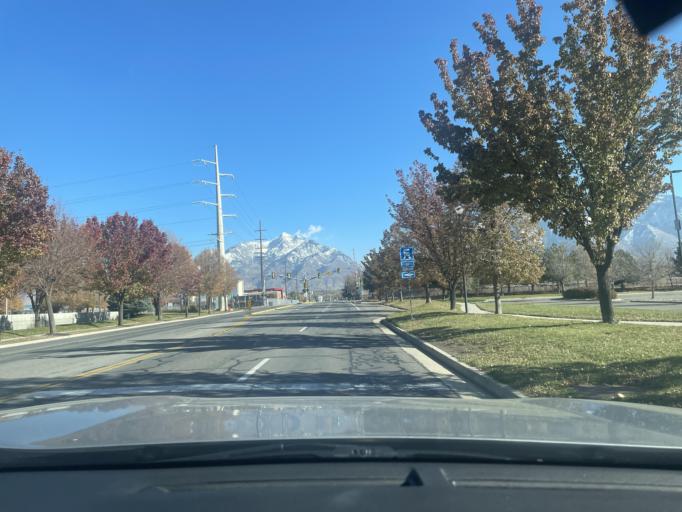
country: US
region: Utah
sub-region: Salt Lake County
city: Sandy City
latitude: 40.5805
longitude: -111.8879
